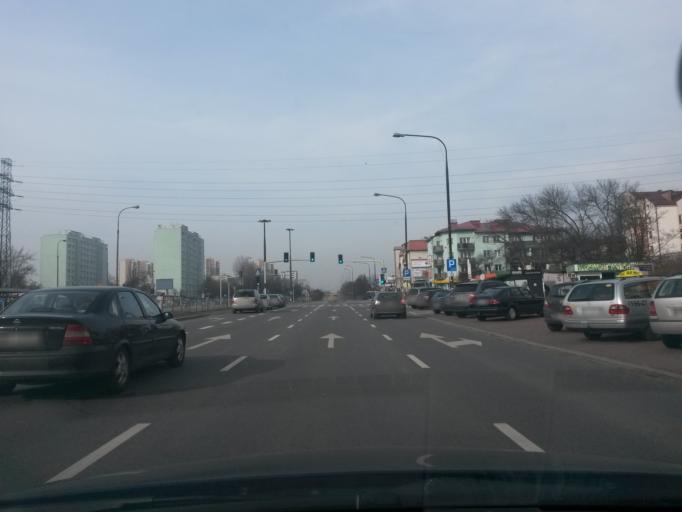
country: PL
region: Masovian Voivodeship
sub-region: Warszawa
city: Wilanow
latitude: 52.1747
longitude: 21.0635
